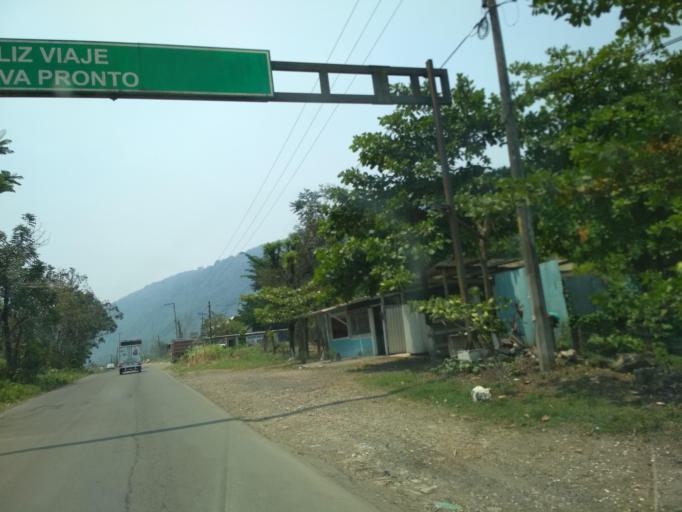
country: MX
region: Veracruz
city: Tezonapa
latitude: 18.6120
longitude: -96.6939
